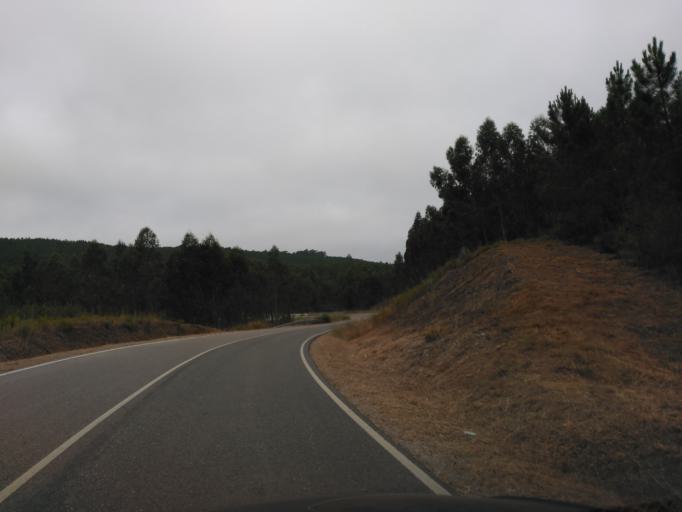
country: PT
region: Santarem
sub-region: Abrantes
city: Alferrarede
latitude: 39.5666
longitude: -8.1330
